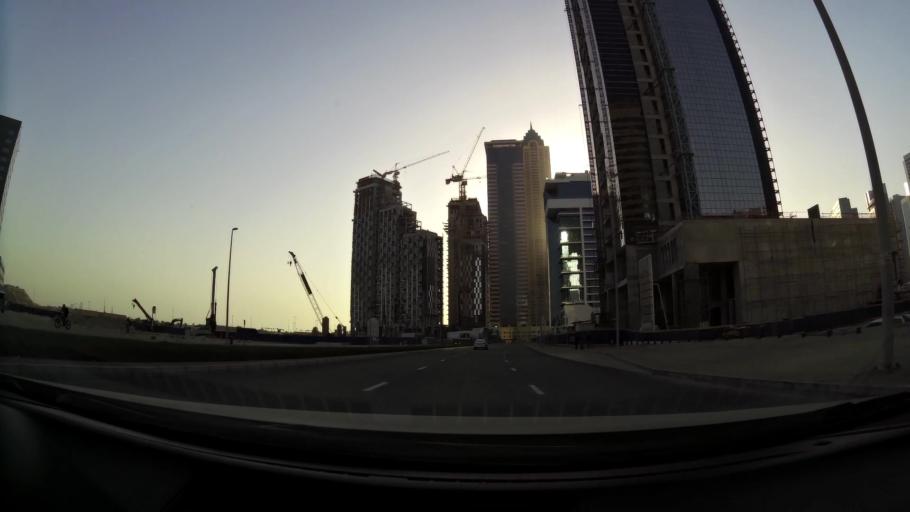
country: AE
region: Dubai
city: Dubai
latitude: 25.1802
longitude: 55.2672
